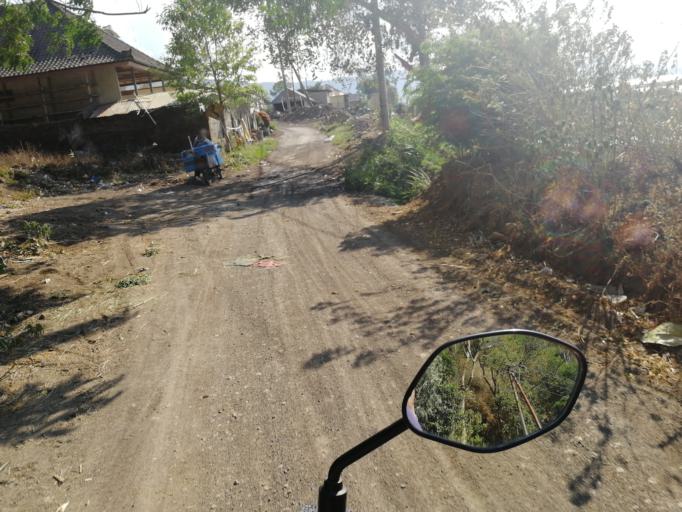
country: ID
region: Bali
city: Banjar Trunyan
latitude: -8.2628
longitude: 115.4225
